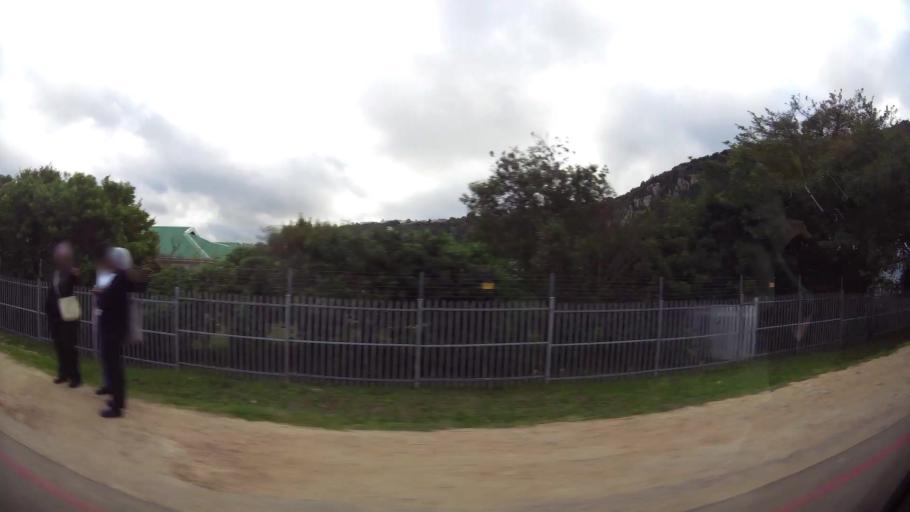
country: ZA
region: Western Cape
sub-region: Eden District Municipality
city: Plettenberg Bay
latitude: -34.0614
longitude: 23.3719
